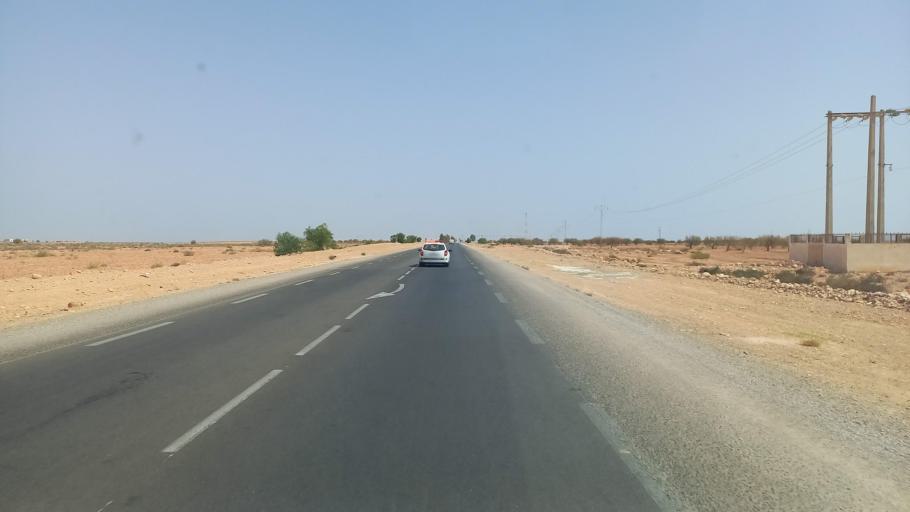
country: TN
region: Madanin
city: Medenine
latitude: 33.3782
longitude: 10.6975
